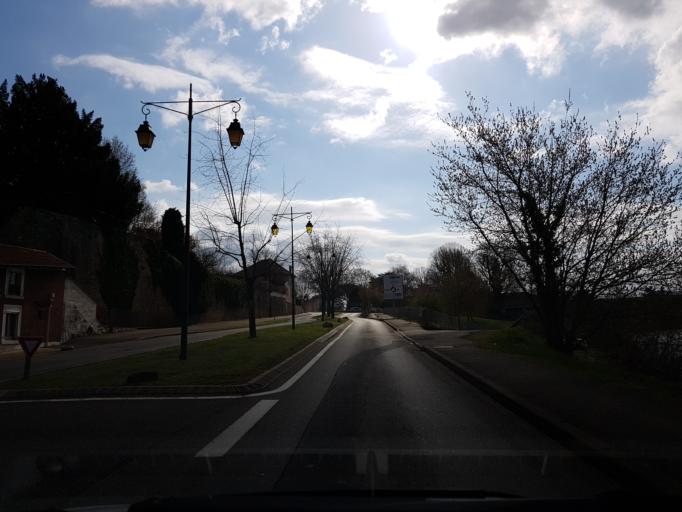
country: FR
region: Rhone-Alpes
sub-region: Departement de l'Ain
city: Trevoux
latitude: 45.9390
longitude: 4.7784
